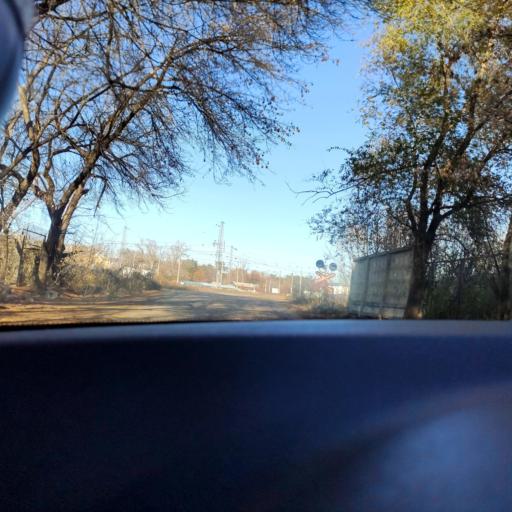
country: RU
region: Samara
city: Samara
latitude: 53.2025
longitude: 50.2480
